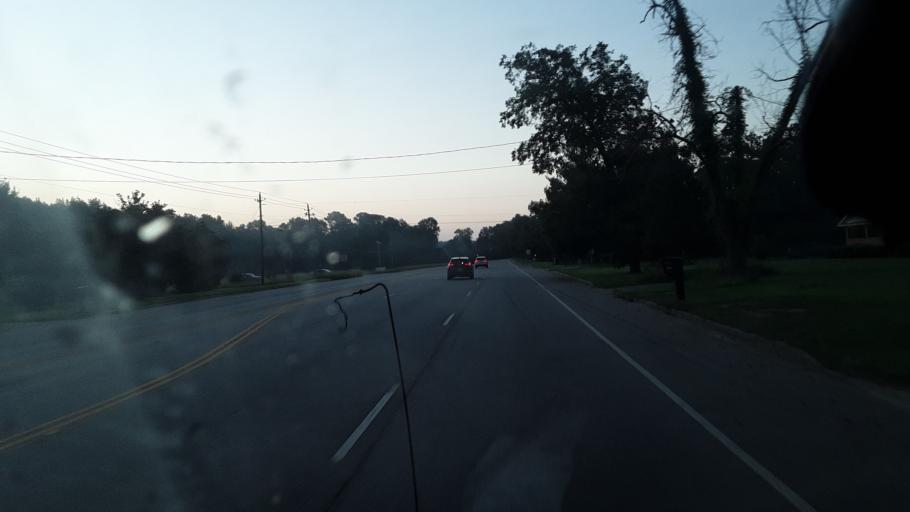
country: US
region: South Carolina
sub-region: Sumter County
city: Lakewood
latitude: 33.8723
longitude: -80.3311
